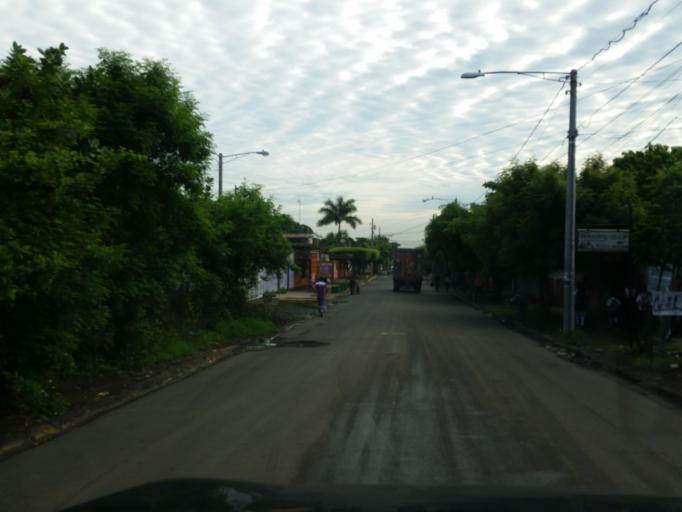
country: NI
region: Managua
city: Managua
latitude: 12.1131
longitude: -86.2035
